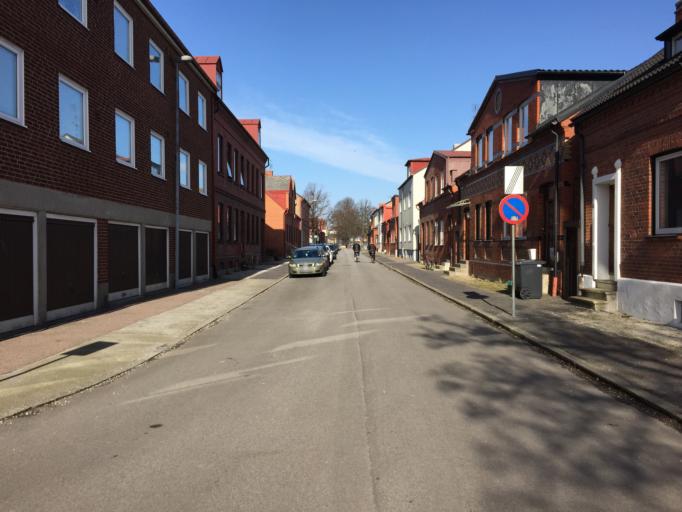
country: SE
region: Skane
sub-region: Trelleborgs Kommun
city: Trelleborg
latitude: 55.3765
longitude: 13.1611
